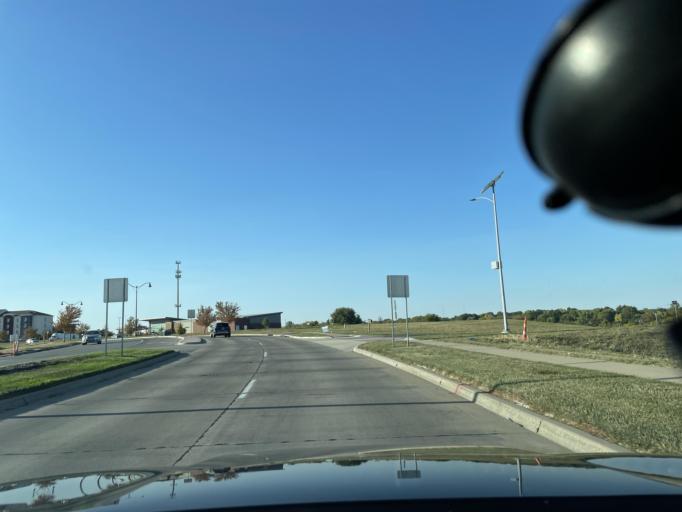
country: US
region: Missouri
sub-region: Andrew County
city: Country Club Village
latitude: 39.8152
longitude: -94.8076
